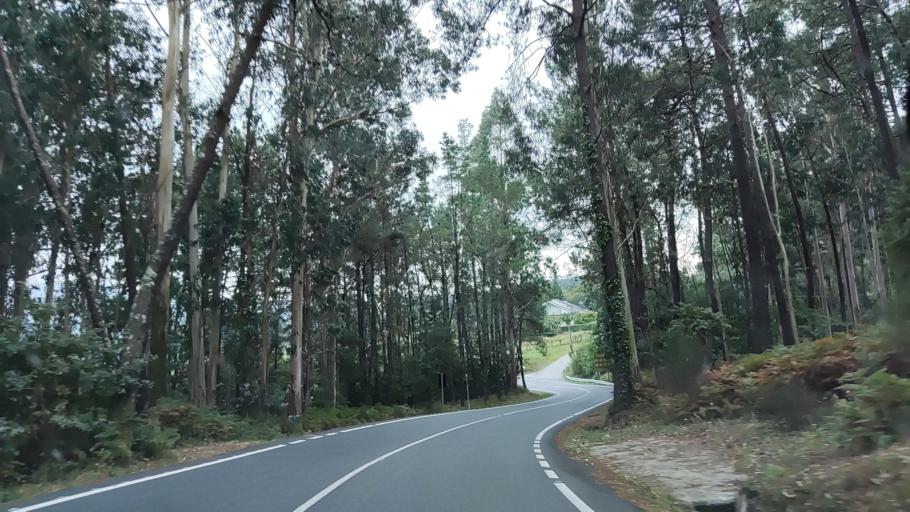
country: ES
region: Galicia
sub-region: Provincia de Pontevedra
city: Catoira
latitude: 42.6907
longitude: -8.7333
